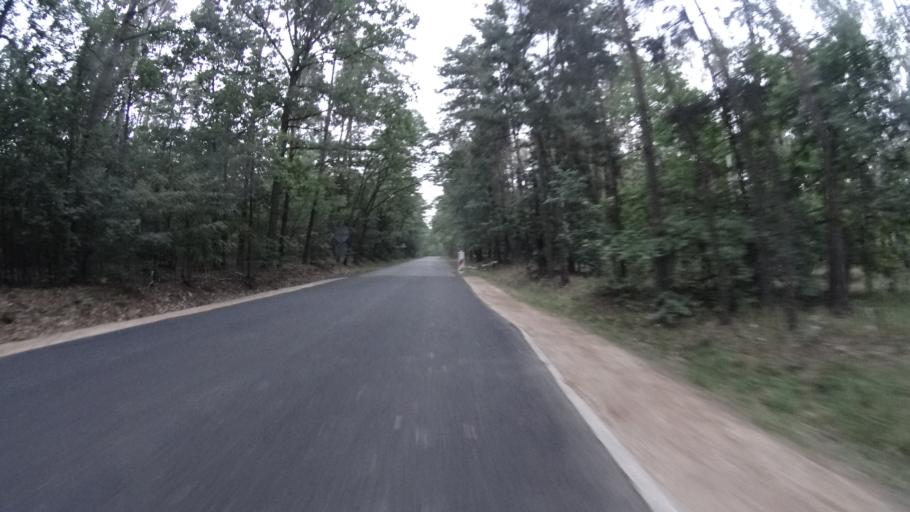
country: PL
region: Masovian Voivodeship
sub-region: Powiat warszawski zachodni
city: Stare Babice
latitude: 52.2716
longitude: 20.8339
